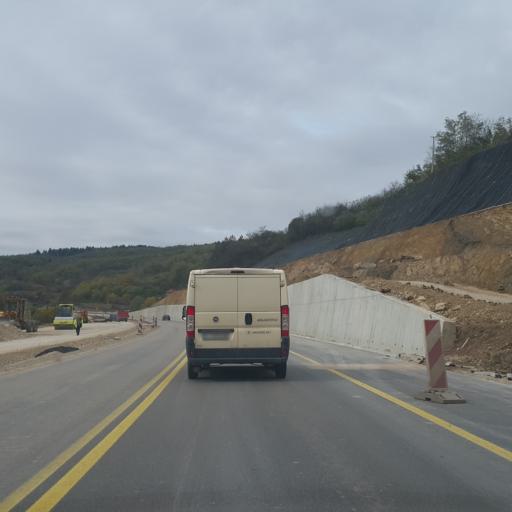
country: RS
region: Central Serbia
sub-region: Pirotski Okrug
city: Bela Palanka
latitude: 43.2319
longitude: 22.4579
